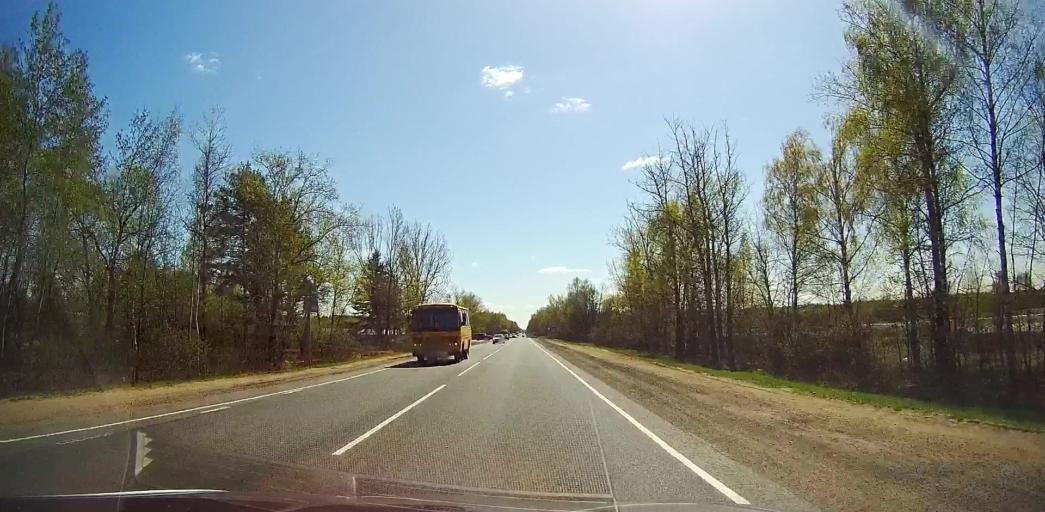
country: RU
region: Moskovskaya
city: Gzhel'
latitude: 55.5731
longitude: 38.3909
